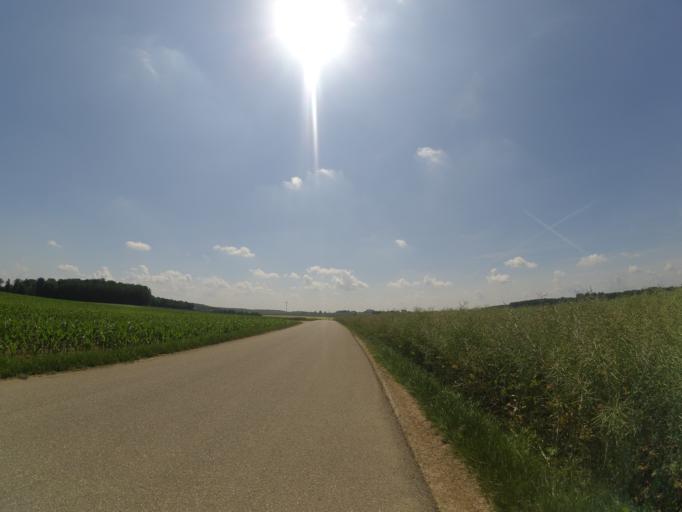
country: DE
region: Baden-Wuerttemberg
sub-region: Tuebingen Region
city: Bernstadt
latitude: 48.4684
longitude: 10.0188
